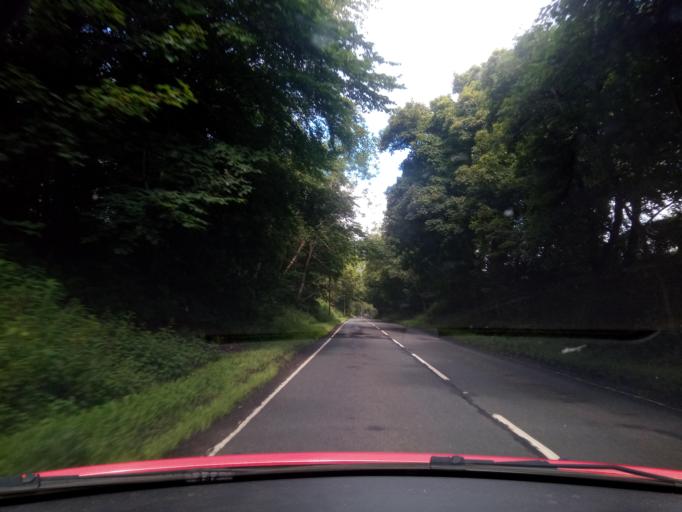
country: GB
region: Scotland
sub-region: The Scottish Borders
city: Lauder
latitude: 55.7220
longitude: -2.7246
